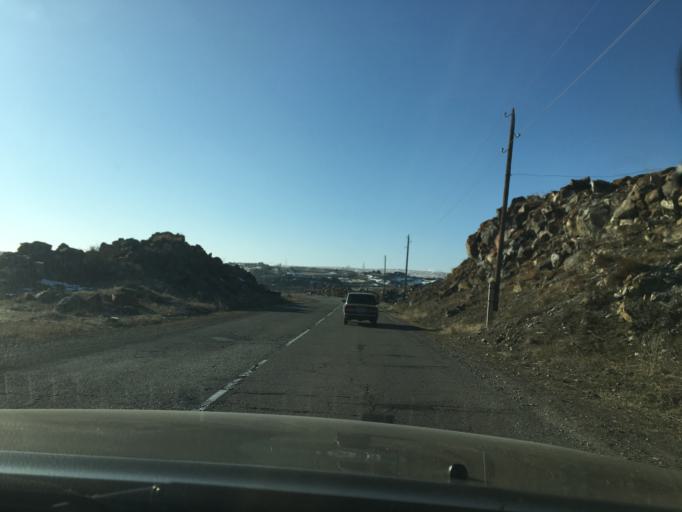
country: AM
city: Lchap'
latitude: 40.4311
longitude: 45.1015
